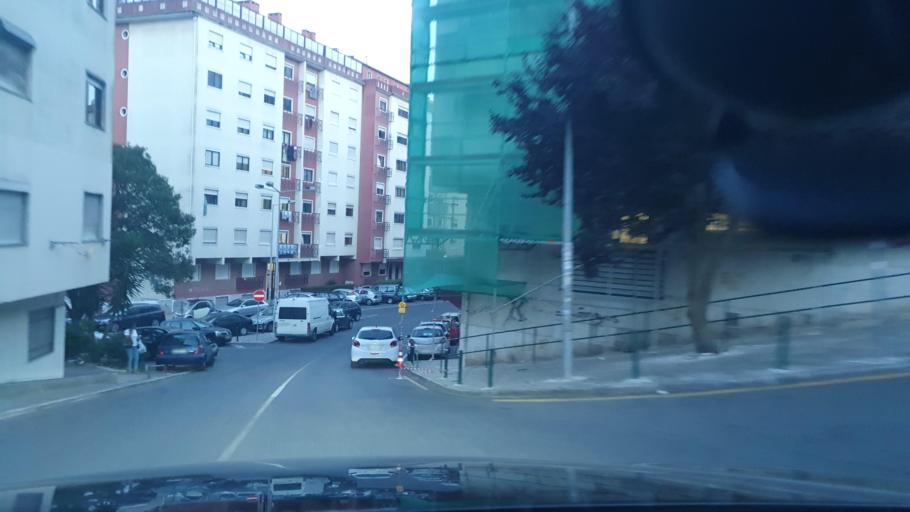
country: PT
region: Lisbon
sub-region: Sintra
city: Queluz
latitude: 38.7655
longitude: -9.2599
